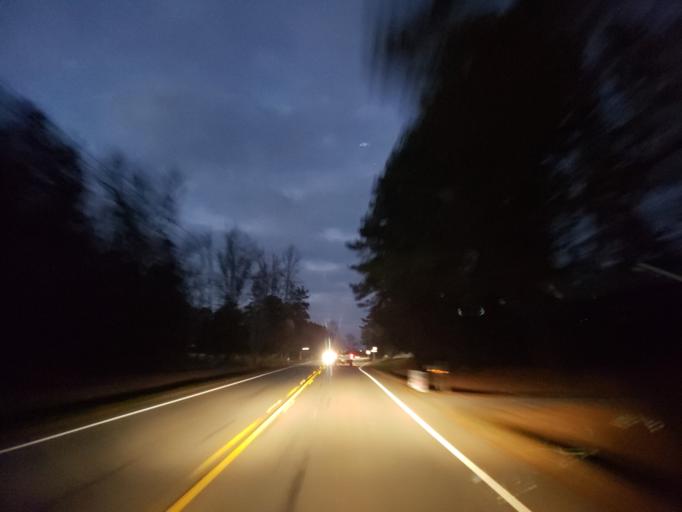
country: US
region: Georgia
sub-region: Polk County
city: Rockmart
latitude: 33.9048
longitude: -84.9960
